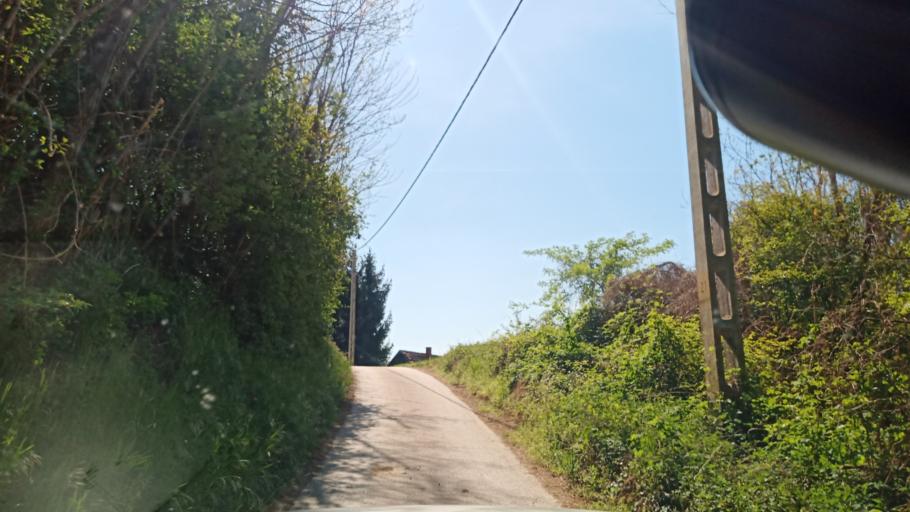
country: HU
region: Zala
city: Heviz
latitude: 46.7724
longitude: 17.0968
